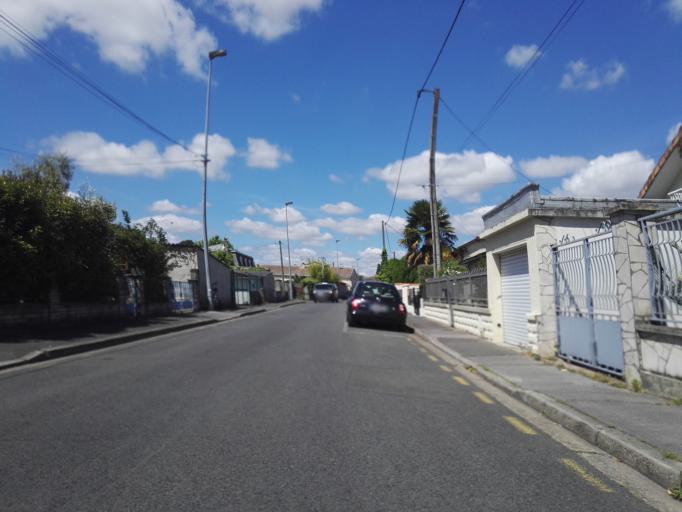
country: FR
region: Aquitaine
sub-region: Departement de la Gironde
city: Begles
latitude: 44.8007
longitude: -0.5638
